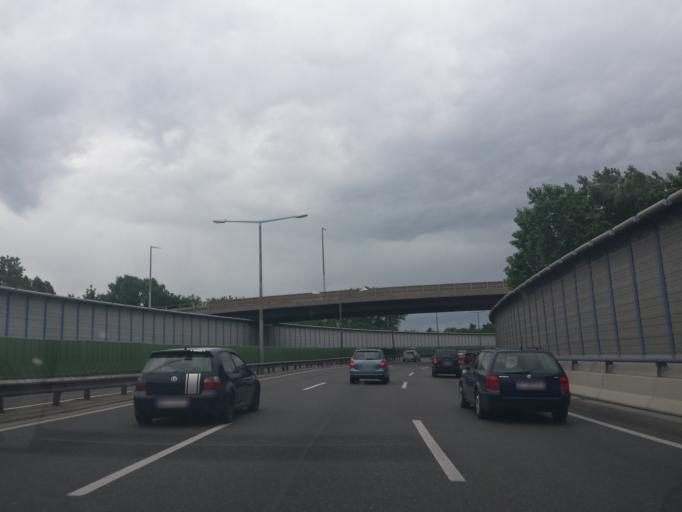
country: AT
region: Vienna
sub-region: Wien Stadt
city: Vienna
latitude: 48.1724
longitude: 16.3987
